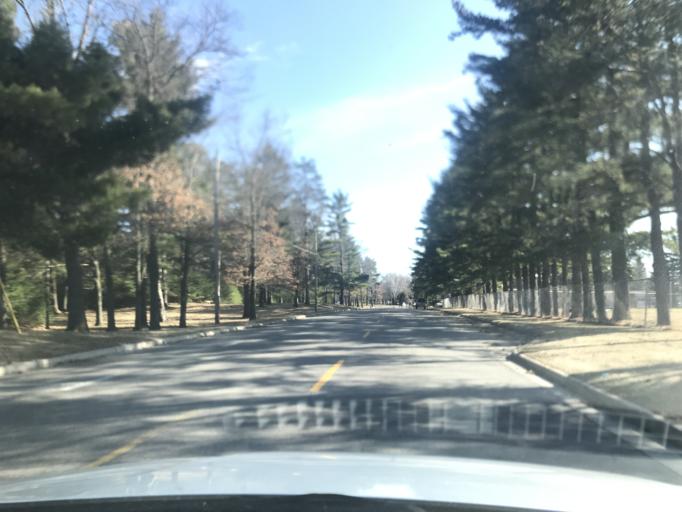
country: US
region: Wisconsin
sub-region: Marinette County
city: Marinette
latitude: 45.0912
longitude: -87.6398
